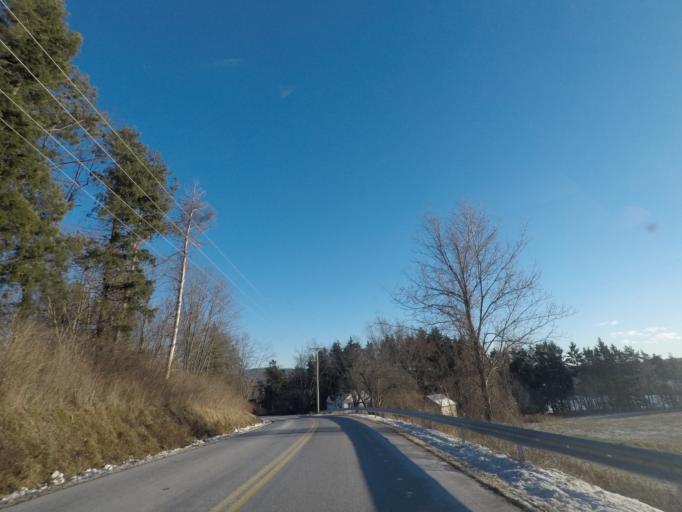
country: US
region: New York
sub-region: Rensselaer County
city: Poestenkill
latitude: 42.7084
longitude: -73.5862
